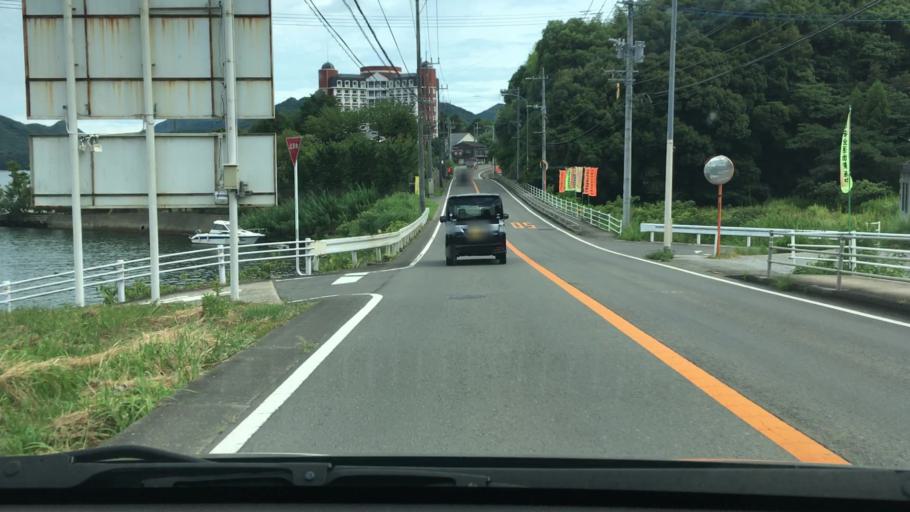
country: JP
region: Nagasaki
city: Togitsu
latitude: 32.8811
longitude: 129.7893
